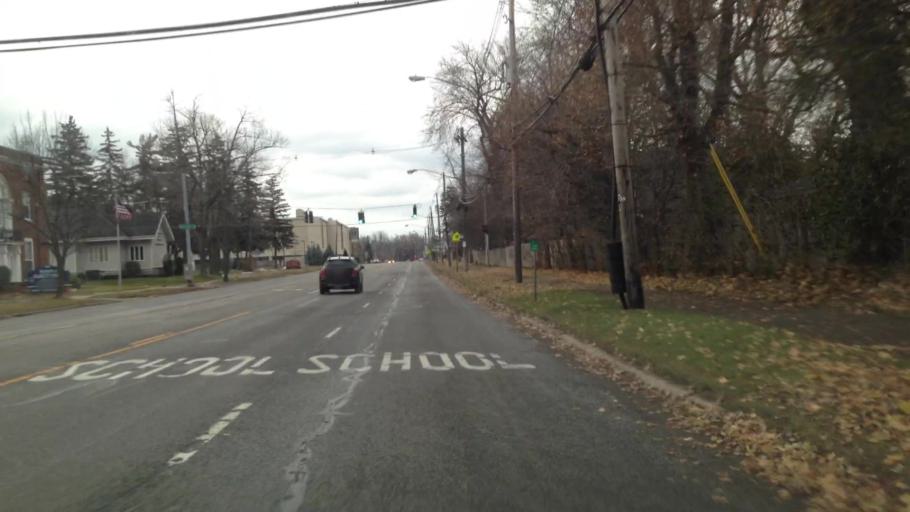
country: US
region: New York
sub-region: Erie County
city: Eggertsville
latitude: 42.9615
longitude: -78.8084
